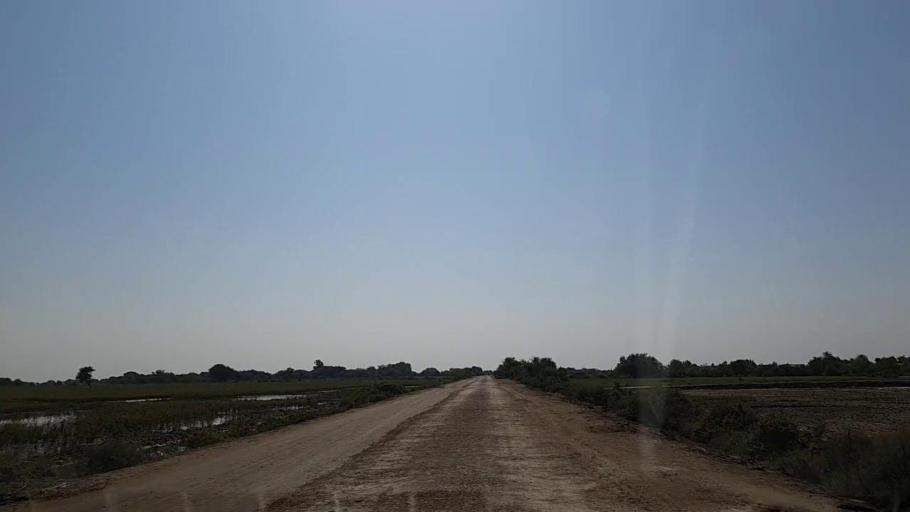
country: PK
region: Sindh
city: Chuhar Jamali
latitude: 24.5187
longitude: 68.0943
